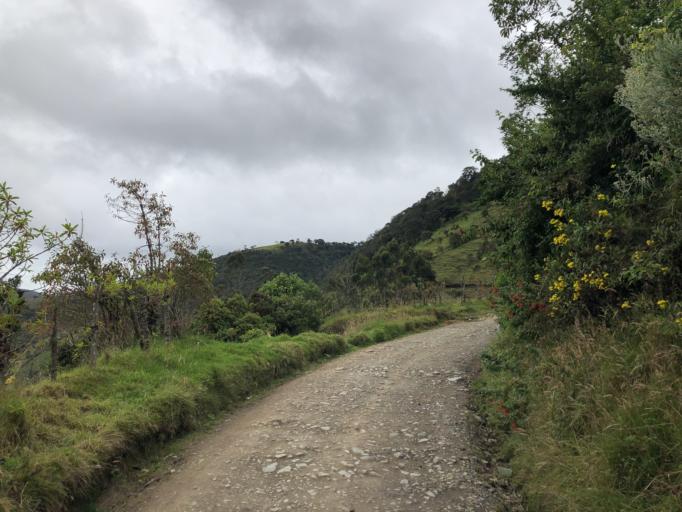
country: CO
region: Cauca
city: Totoro
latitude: 2.5018
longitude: -76.3585
